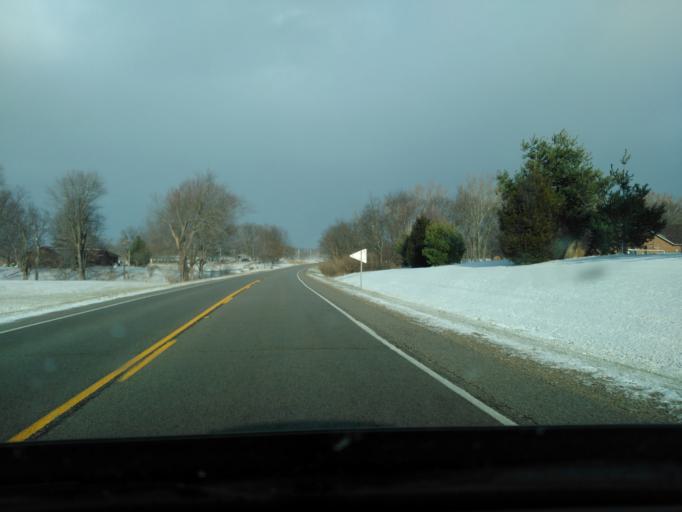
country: US
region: Illinois
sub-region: Madison County
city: Highland
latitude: 38.7633
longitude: -89.6570
